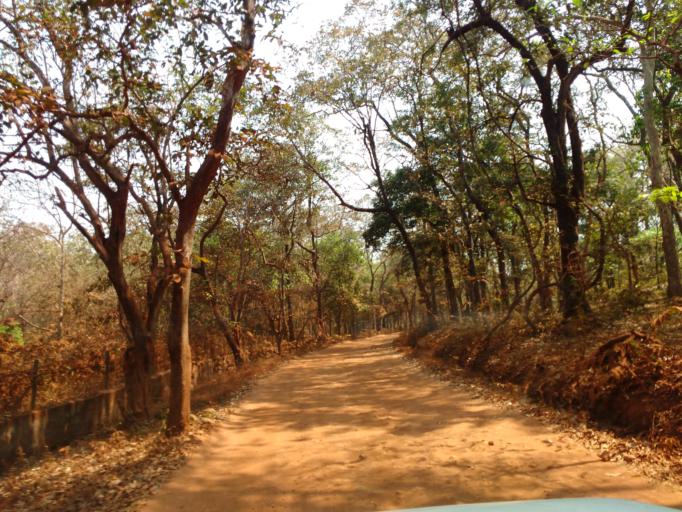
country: IN
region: Goa
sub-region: South Goa
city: Sanguem
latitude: 15.3411
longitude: 74.2520
